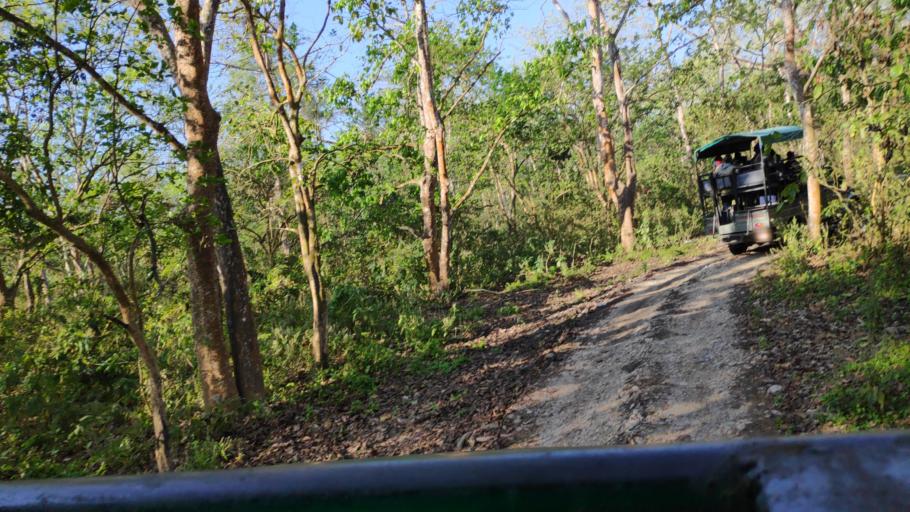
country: NP
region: Central Region
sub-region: Narayani Zone
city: Bharatpur
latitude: 27.5588
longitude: 84.5508
